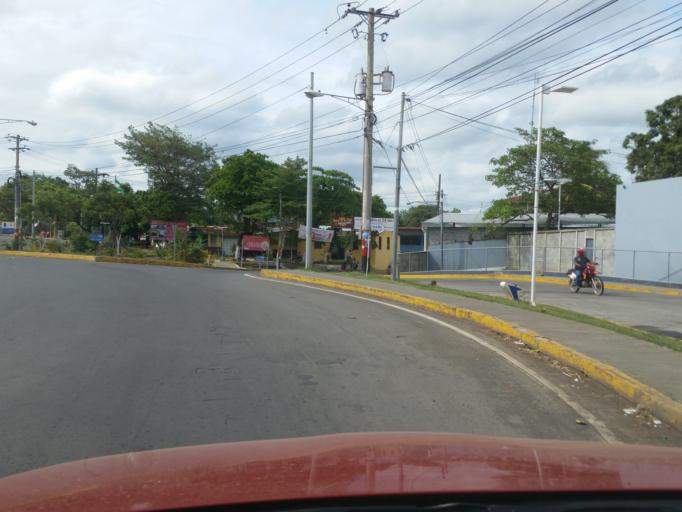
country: NI
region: Masaya
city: Masaya
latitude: 11.9881
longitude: -86.0967
